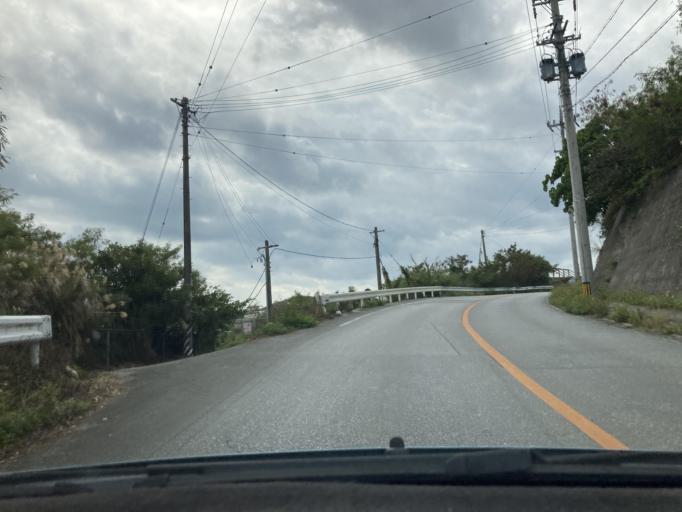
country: JP
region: Okinawa
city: Ginowan
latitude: 26.2137
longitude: 127.7400
